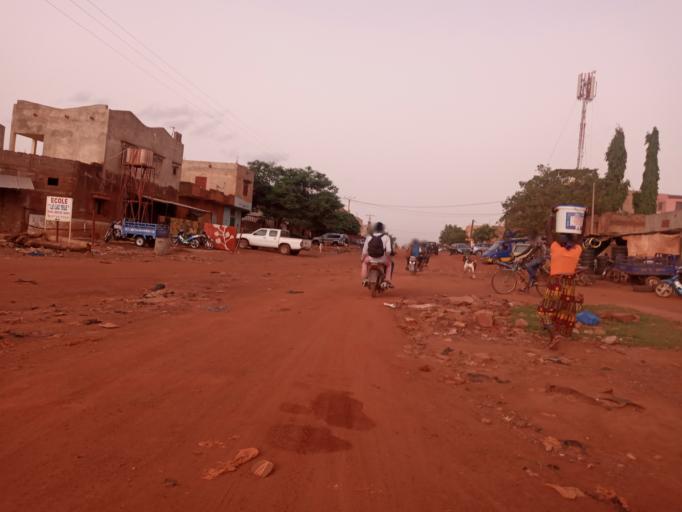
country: ML
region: Bamako
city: Bamako
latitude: 12.5581
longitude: -7.9877
